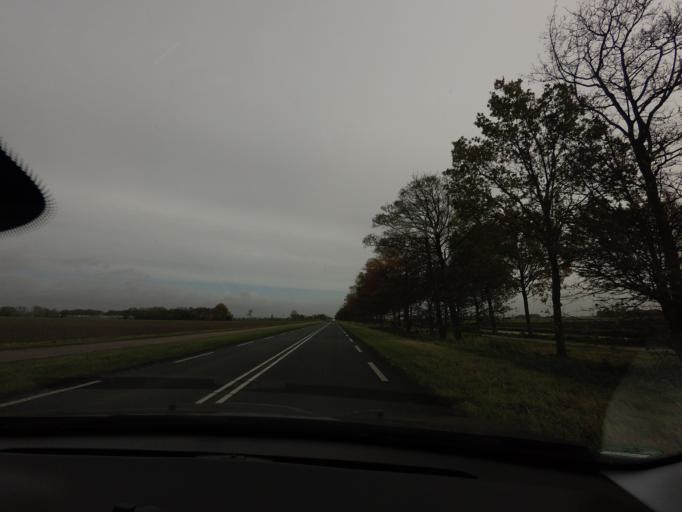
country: NL
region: Flevoland
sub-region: Gemeente Noordoostpolder
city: Emmeloord
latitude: 52.7087
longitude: 5.7971
